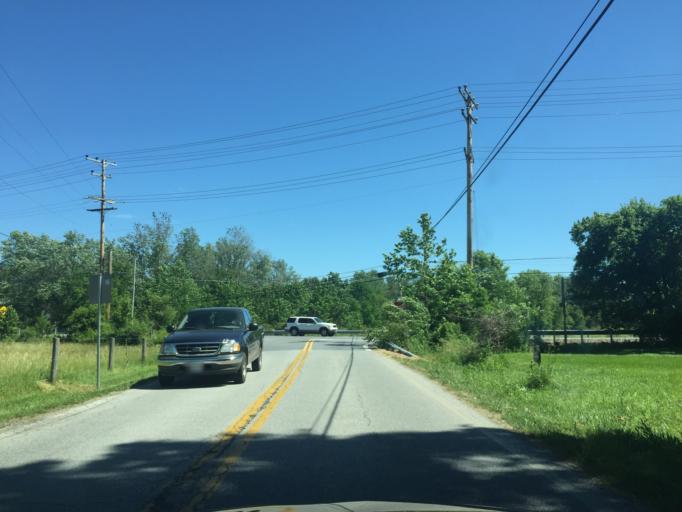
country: US
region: Maryland
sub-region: Carroll County
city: Hampstead
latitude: 39.6103
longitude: -76.8824
